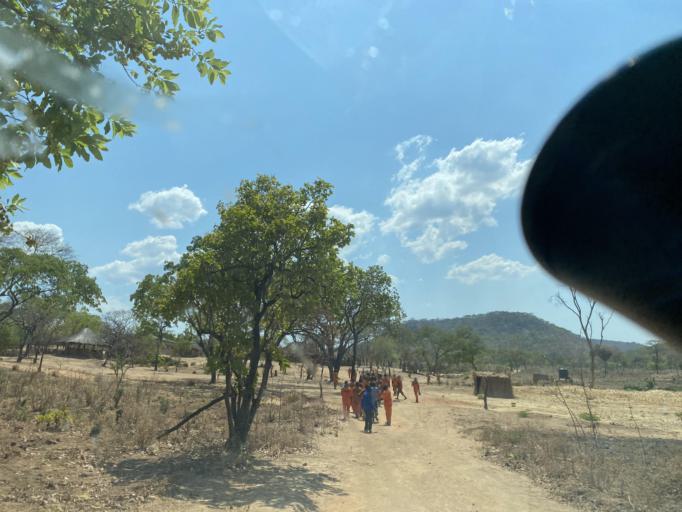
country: ZM
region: Lusaka
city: Chongwe
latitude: -15.0837
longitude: 29.4751
